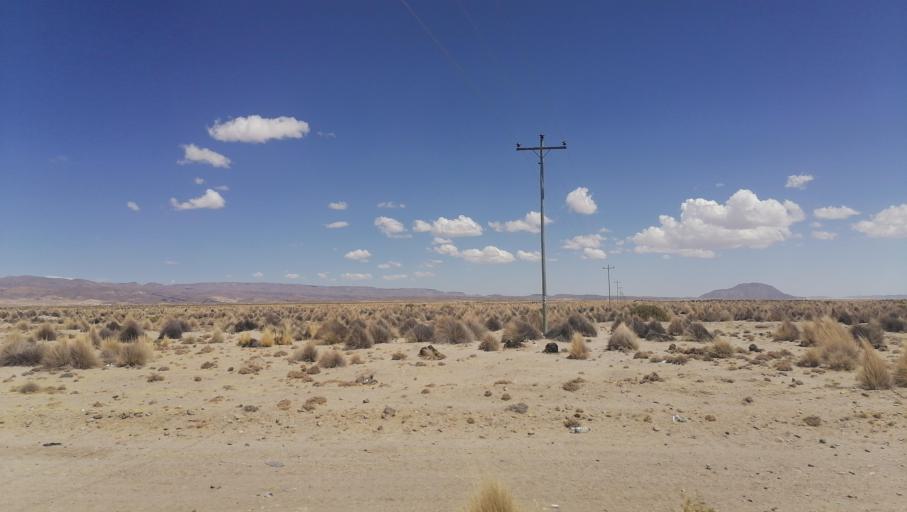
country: BO
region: Oruro
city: Challapata
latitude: -19.1715
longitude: -66.7950
